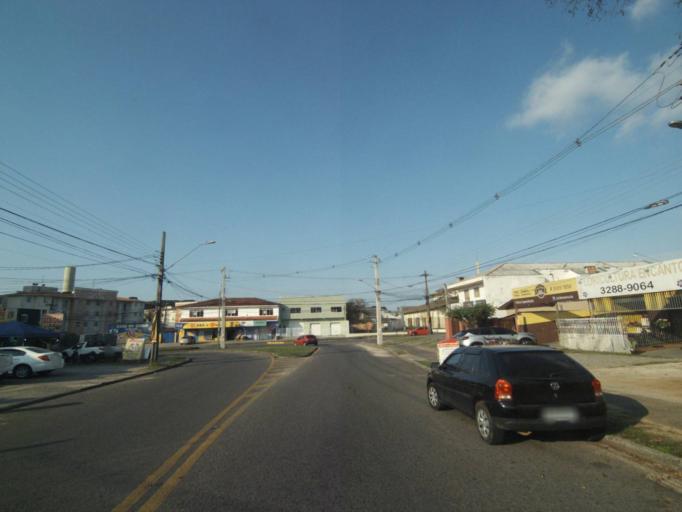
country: BR
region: Parana
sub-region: Curitiba
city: Curitiba
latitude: -25.4805
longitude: -49.3237
